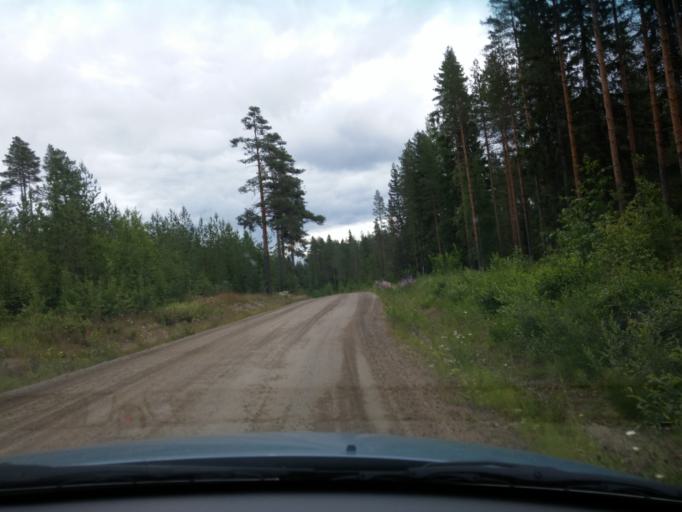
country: FI
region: Central Finland
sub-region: AEaenekoski
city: AEaenekoski
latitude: 62.7636
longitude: 25.6209
